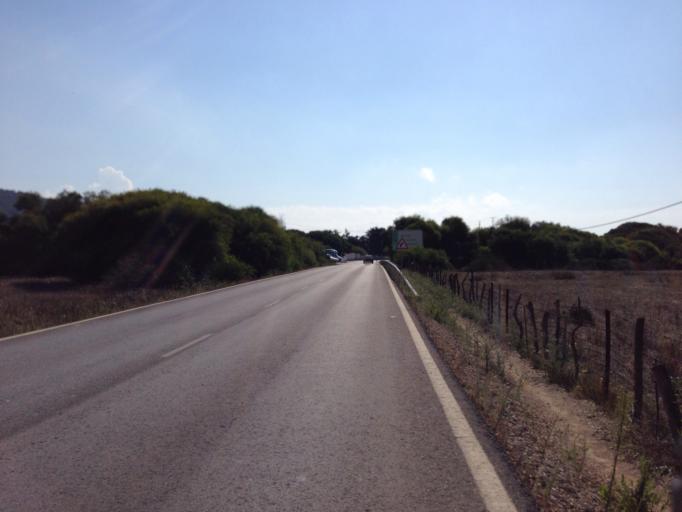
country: ES
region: Andalusia
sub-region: Provincia de Cadiz
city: Vejer de la Frontera
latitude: 36.1912
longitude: -6.0285
